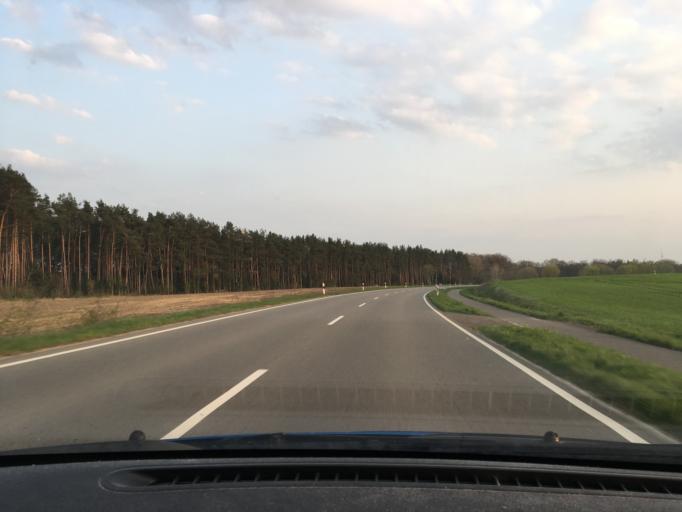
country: DE
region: Lower Saxony
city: Oldendorf
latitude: 53.1498
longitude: 10.2147
